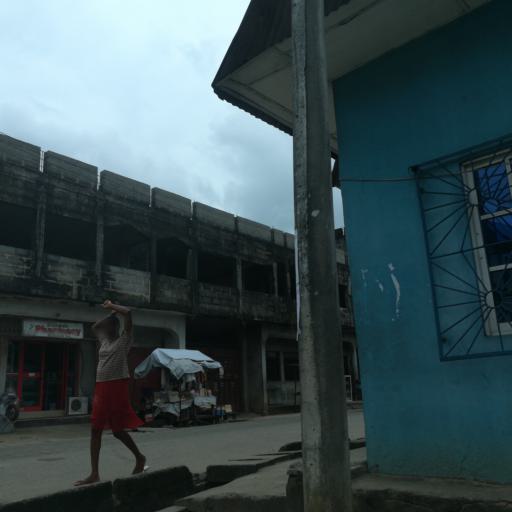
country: NG
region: Rivers
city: Port Harcourt
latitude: 4.8349
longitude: 7.0312
